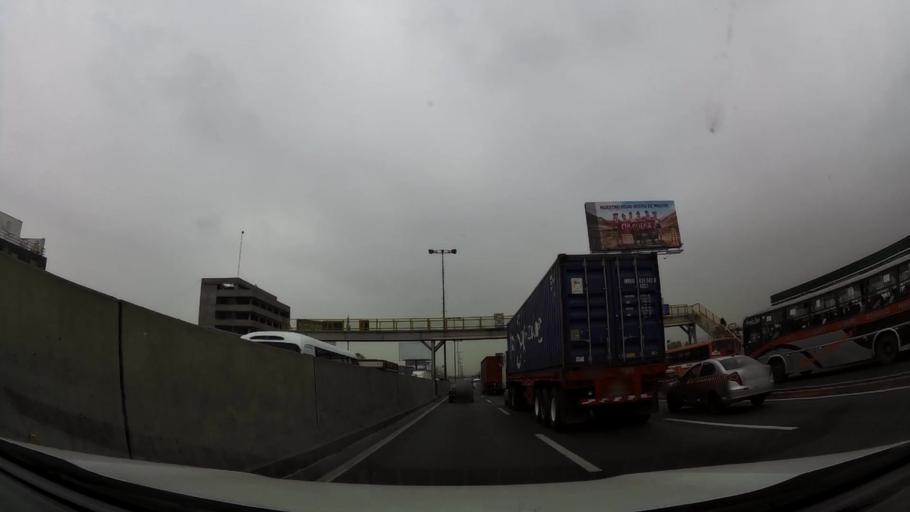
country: PE
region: Lima
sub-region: Lima
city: Independencia
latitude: -12.0232
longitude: -77.0589
